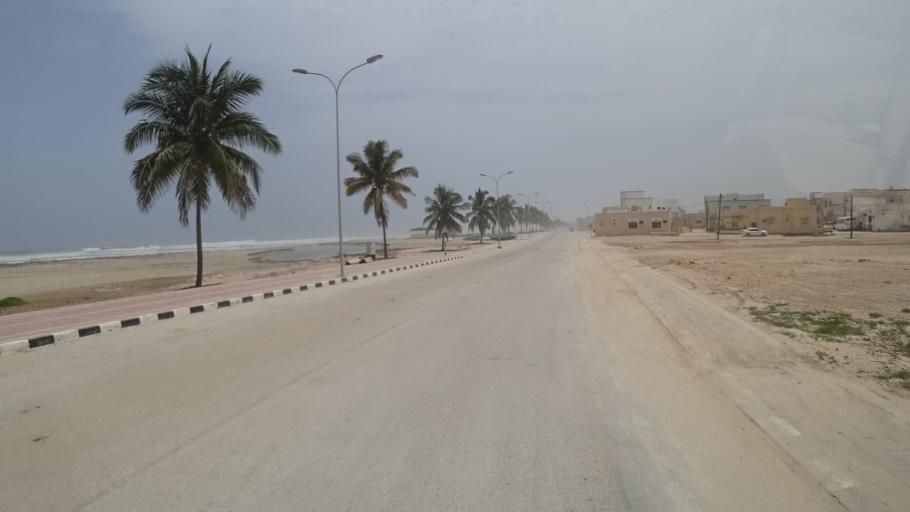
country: OM
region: Zufar
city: Salalah
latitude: 17.0349
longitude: 54.4059
